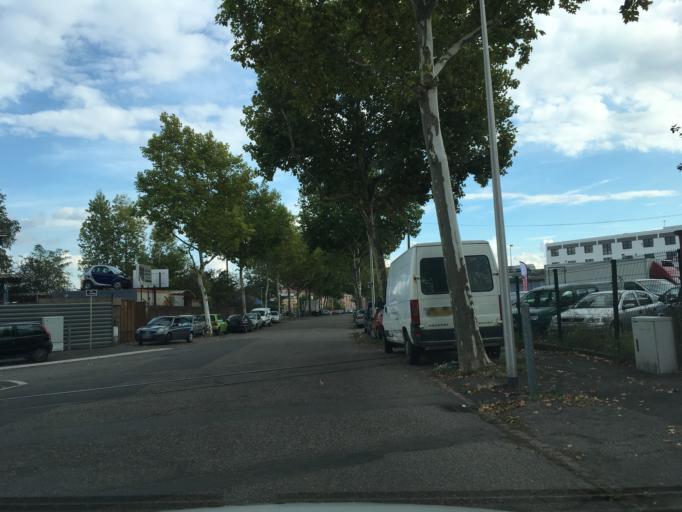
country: FR
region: Alsace
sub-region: Departement du Haut-Rhin
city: Colmar
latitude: 48.0885
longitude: 7.3538
